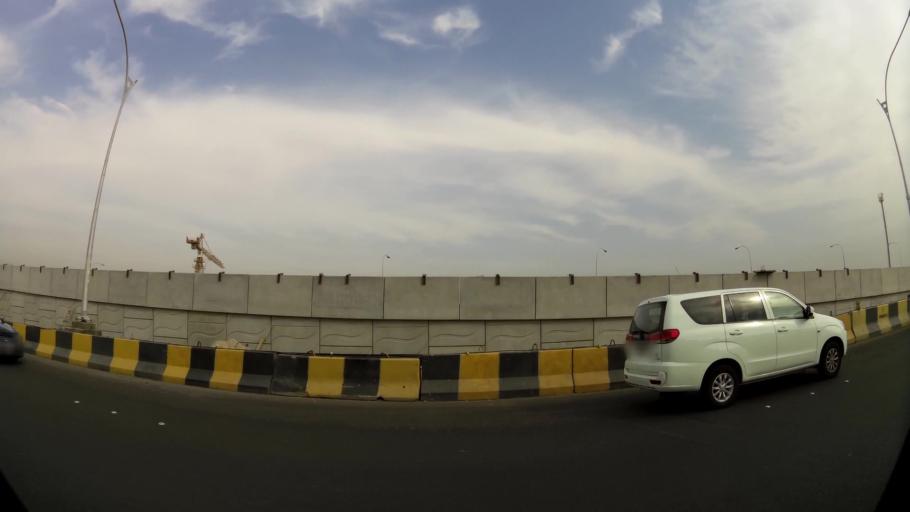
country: KW
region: Al Asimah
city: Ar Rabiyah
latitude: 29.3196
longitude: 47.8322
